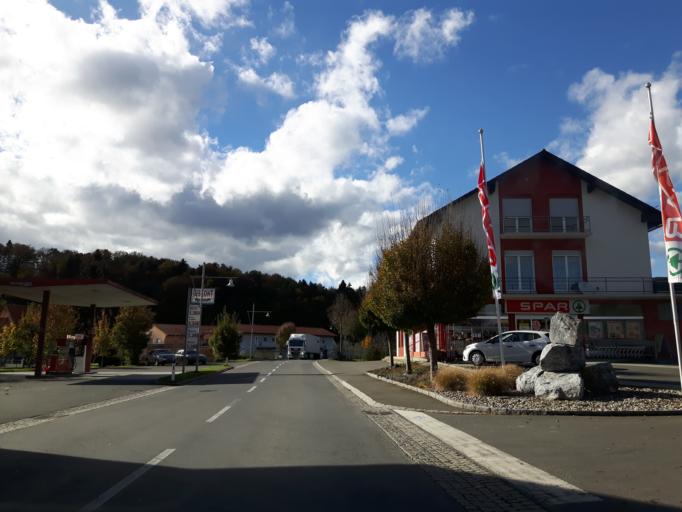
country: AT
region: Styria
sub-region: Politischer Bezirk Suedoststeiermark
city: Paldau
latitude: 46.9413
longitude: 15.7869
